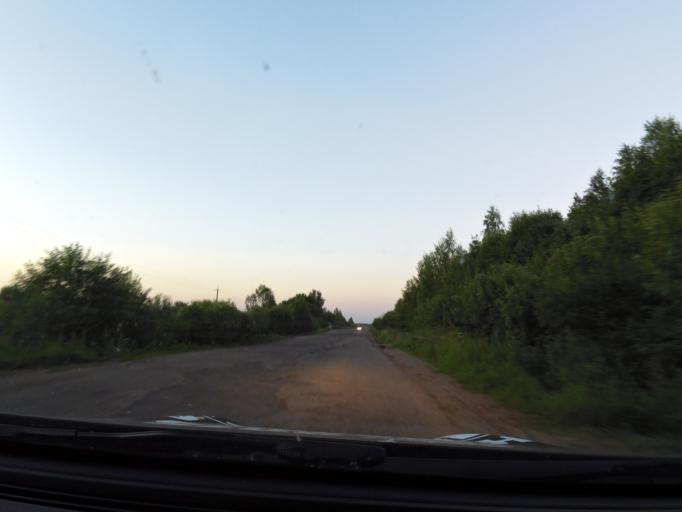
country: RU
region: Kostroma
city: Buy
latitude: 58.4307
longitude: 41.2933
